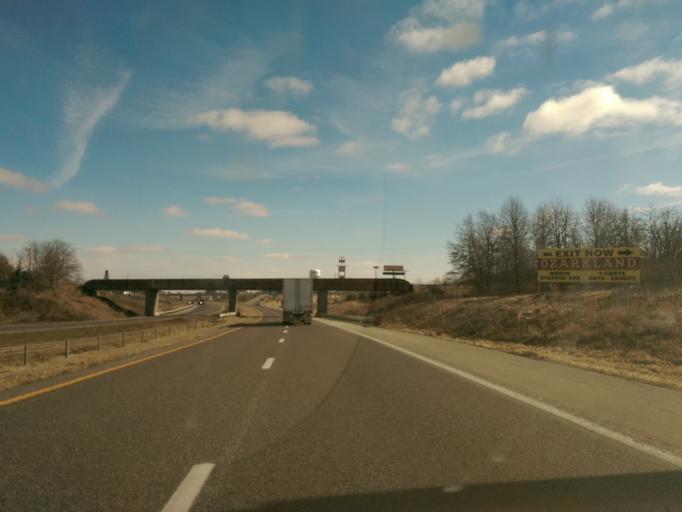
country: US
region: Missouri
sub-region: Callaway County
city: Fulton
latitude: 38.9449
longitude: -91.9490
